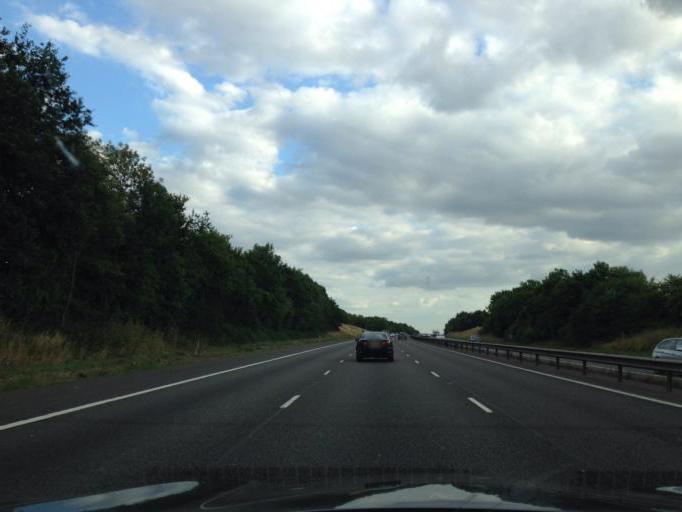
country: GB
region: England
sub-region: Oxfordshire
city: Somerton
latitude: 51.9991
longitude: -1.2693
